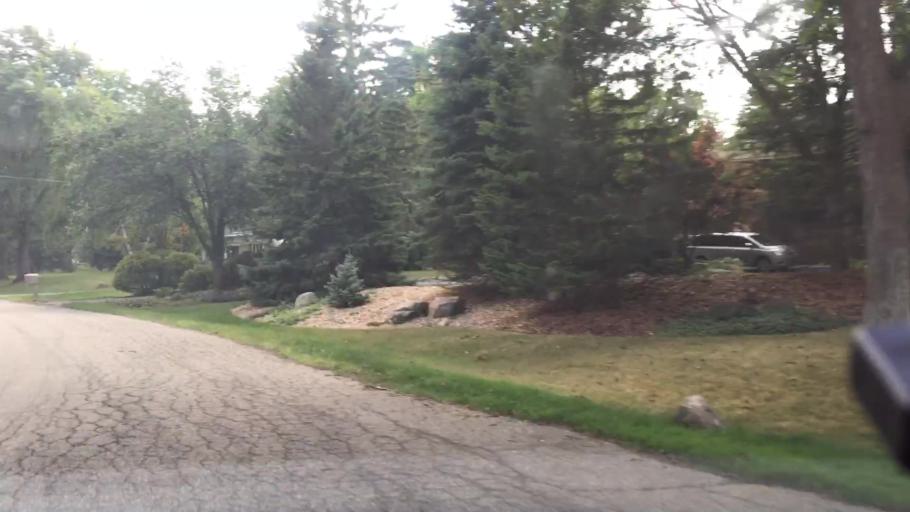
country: US
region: Michigan
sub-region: Oakland County
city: Sylvan Lake
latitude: 42.5709
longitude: -83.3157
